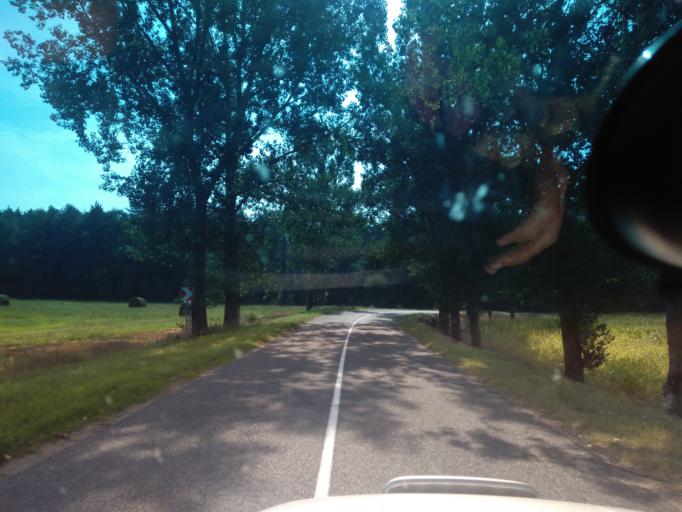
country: BY
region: Minsk
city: Kapyl'
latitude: 53.2751
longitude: 27.2304
